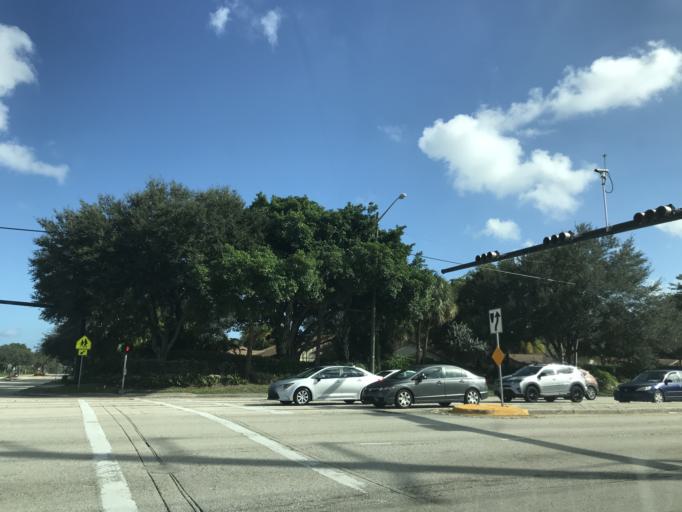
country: US
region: Florida
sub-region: Broward County
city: Coconut Creek
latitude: 26.2596
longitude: -80.1866
